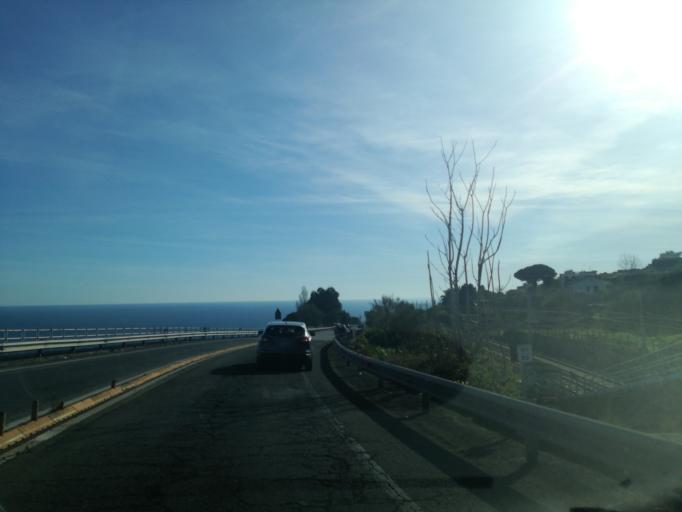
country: IT
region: Sicily
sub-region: Catania
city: Acireale
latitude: 37.6166
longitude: 15.1702
